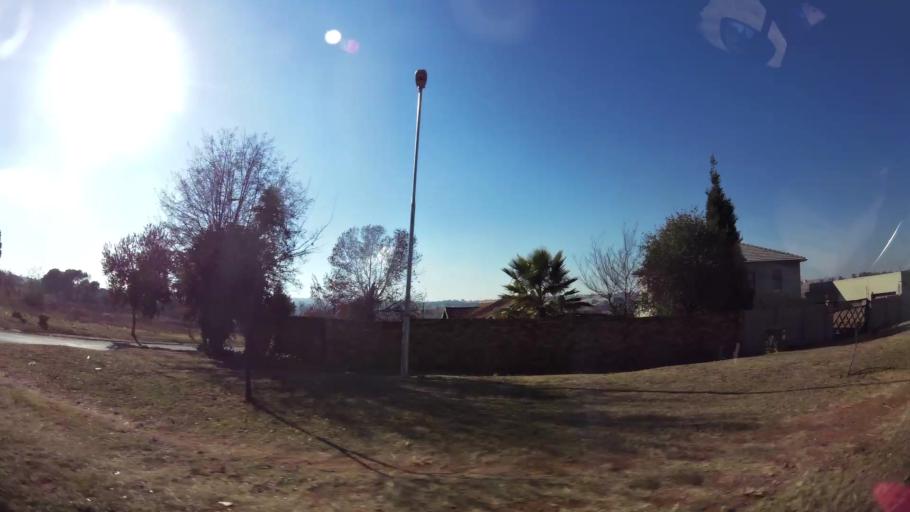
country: ZA
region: Gauteng
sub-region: City of Johannesburg Metropolitan Municipality
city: Roodepoort
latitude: -26.1600
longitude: 27.8327
